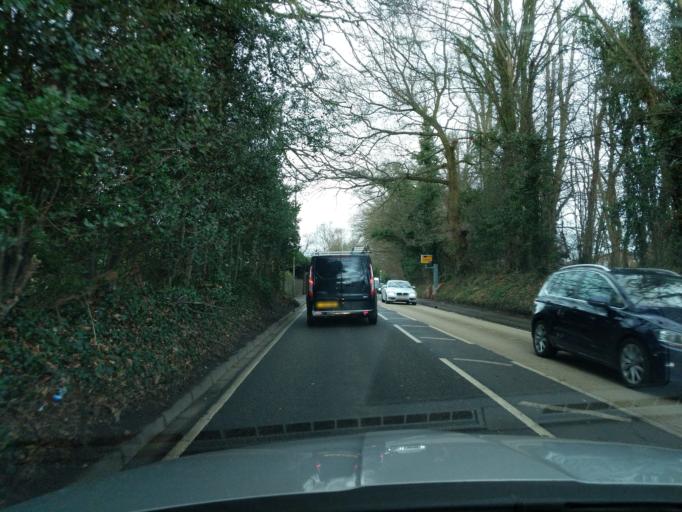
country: GB
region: England
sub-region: Hertfordshire
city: Abbots Langley
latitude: 51.6762
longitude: -0.4219
